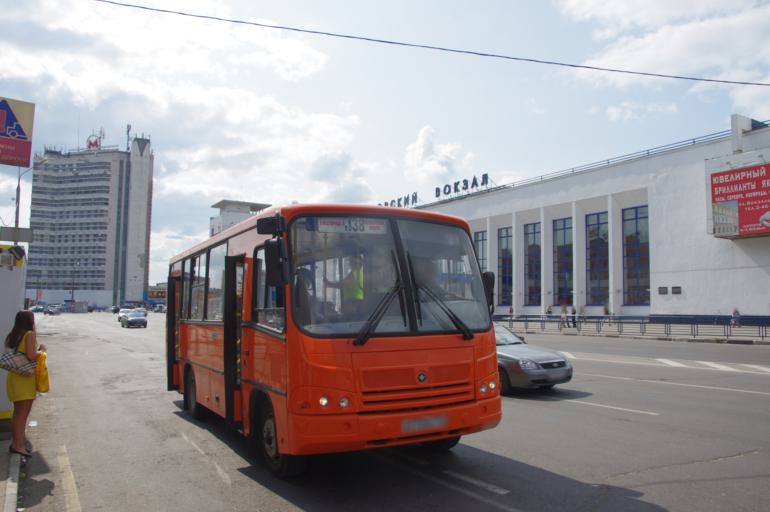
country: RU
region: Nizjnij Novgorod
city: Nizhniy Novgorod
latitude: 56.3217
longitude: 43.9475
